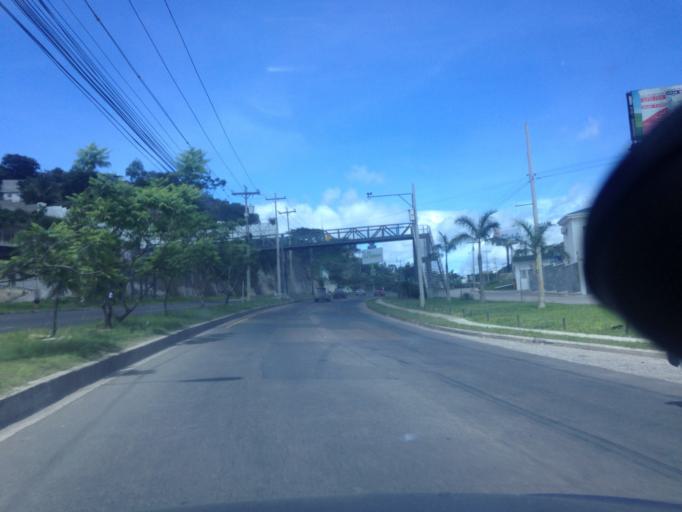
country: HN
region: Francisco Morazan
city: Tegucigalpa
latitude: 14.0513
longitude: -87.2036
